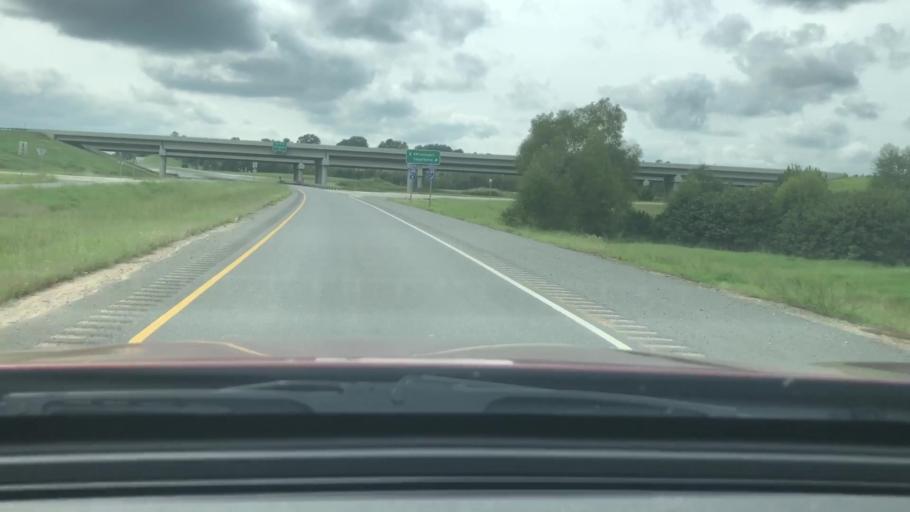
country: US
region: Louisiana
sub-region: Caddo Parish
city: Vivian
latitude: 32.9437
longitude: -93.8955
